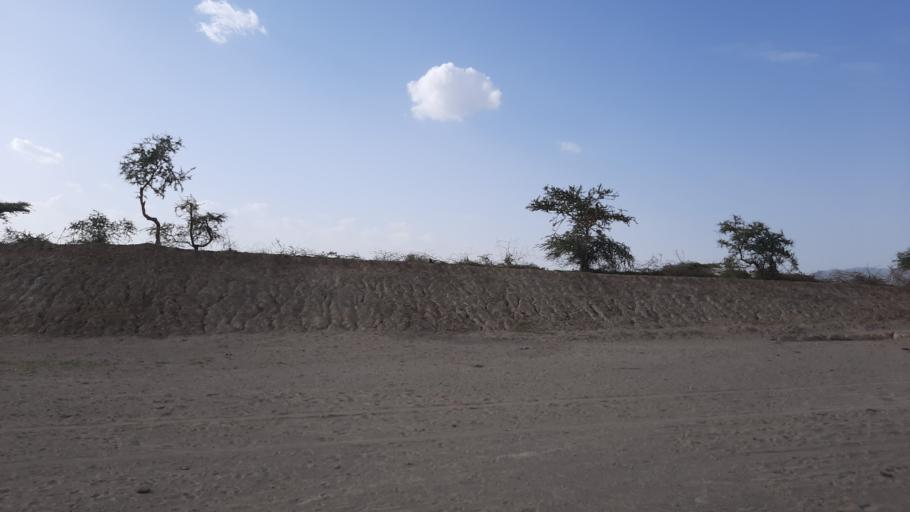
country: ET
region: Oromiya
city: Ziway
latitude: 7.6699
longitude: 38.6792
